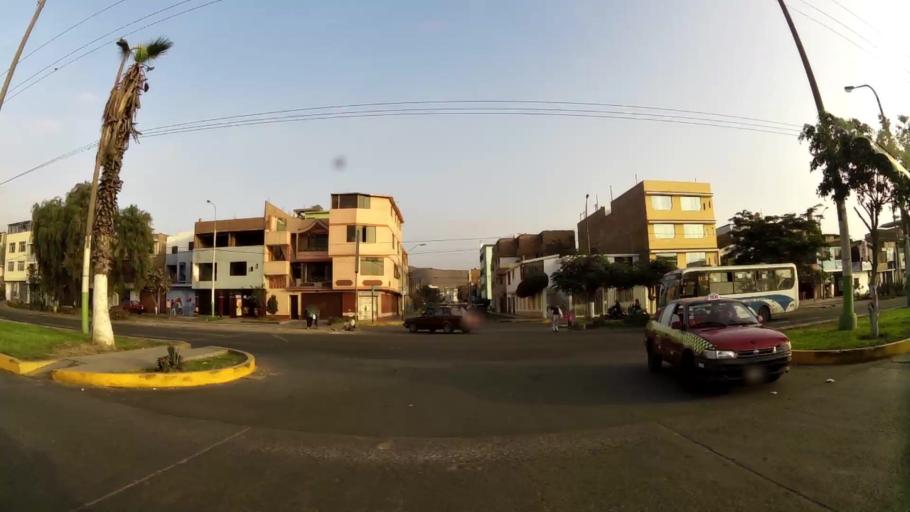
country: PE
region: Lima
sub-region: Lima
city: Independencia
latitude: -11.9918
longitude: -77.0779
